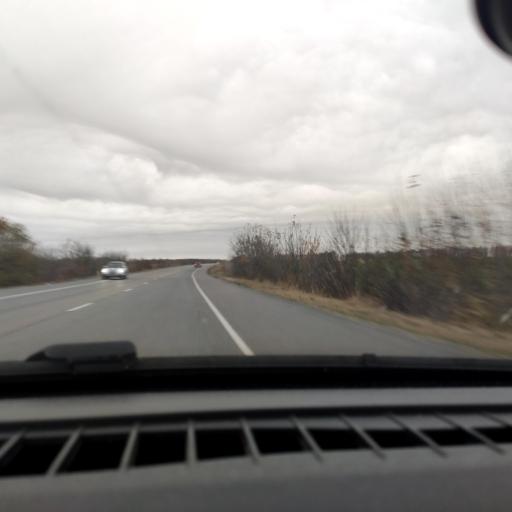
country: RU
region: Voronezj
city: Devitsa
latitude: 51.6102
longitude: 38.9794
